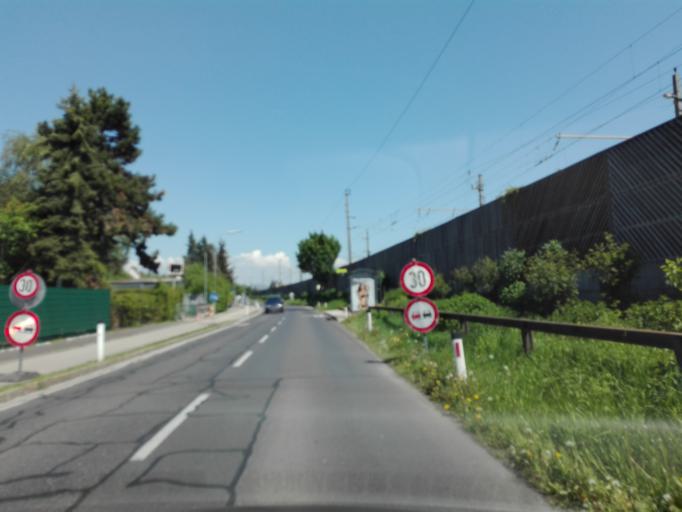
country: AT
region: Upper Austria
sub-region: Politischer Bezirk Linz-Land
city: Traun
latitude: 48.2300
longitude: 14.2577
